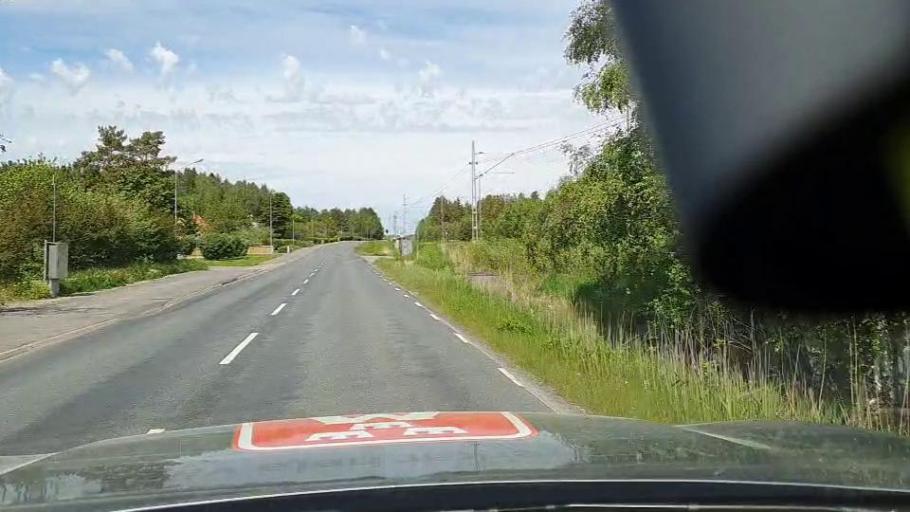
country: SE
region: Soedermanland
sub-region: Eskilstuna Kommun
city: Skogstorp
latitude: 59.2965
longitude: 16.4585
